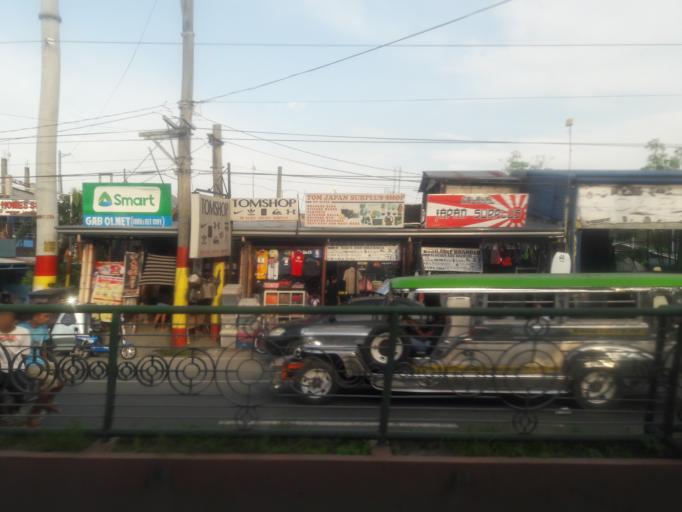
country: PH
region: Calabarzon
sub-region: Province of Cavite
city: Imus
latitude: 14.3846
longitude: 120.9394
